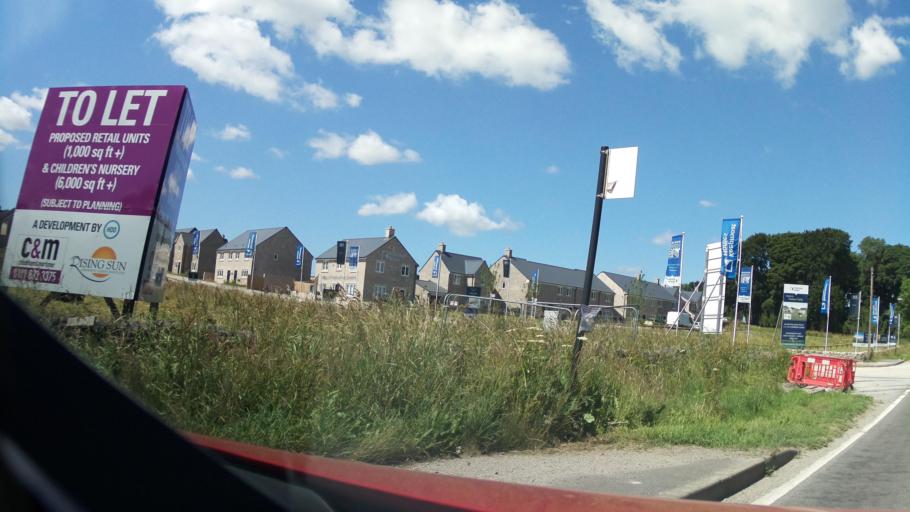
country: GB
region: England
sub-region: Derbyshire
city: Buxton
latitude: 53.2426
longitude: -1.8986
